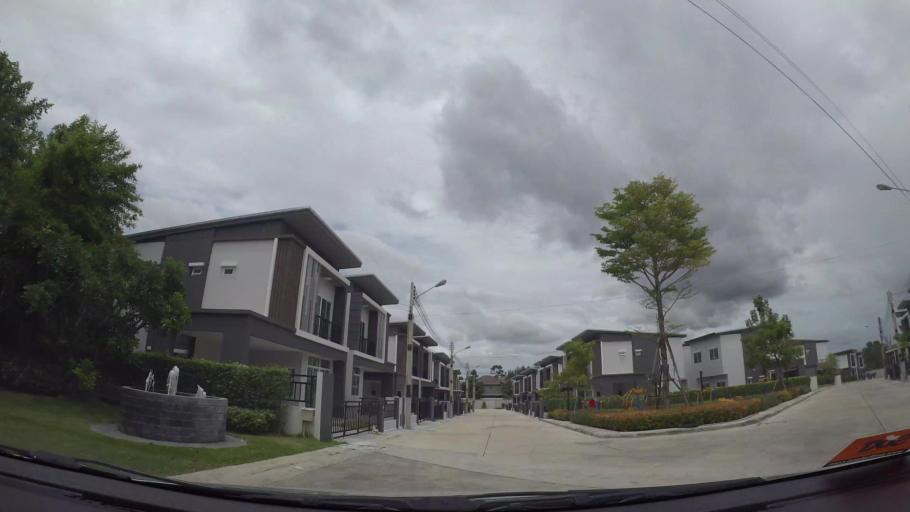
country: TH
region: Chon Buri
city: Si Racha
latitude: 13.1601
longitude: 100.9793
